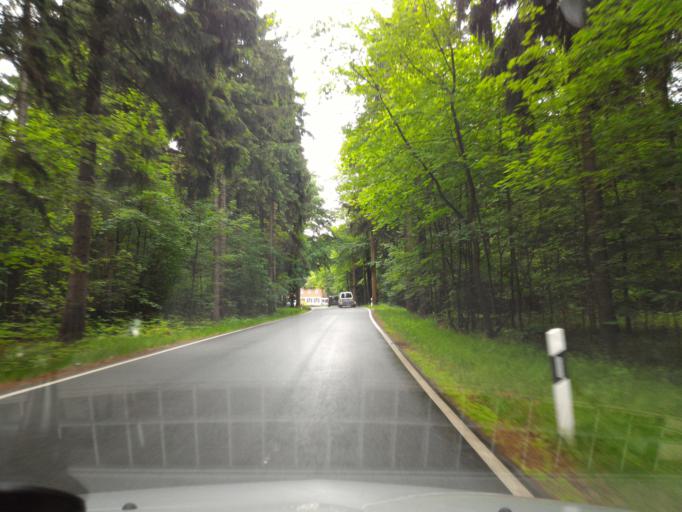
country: DE
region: Saxony
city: Kurort Oybin
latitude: 50.8300
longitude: 14.7827
